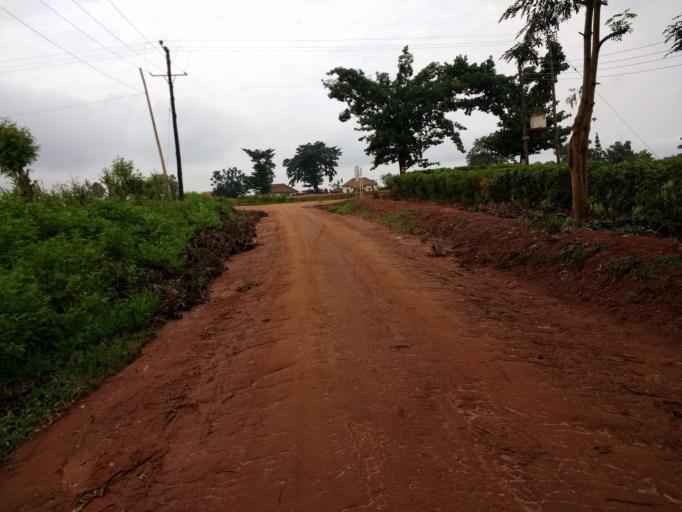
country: UG
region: Eastern Region
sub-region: Mbale District
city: Mbale
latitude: 1.0698
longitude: 34.1682
